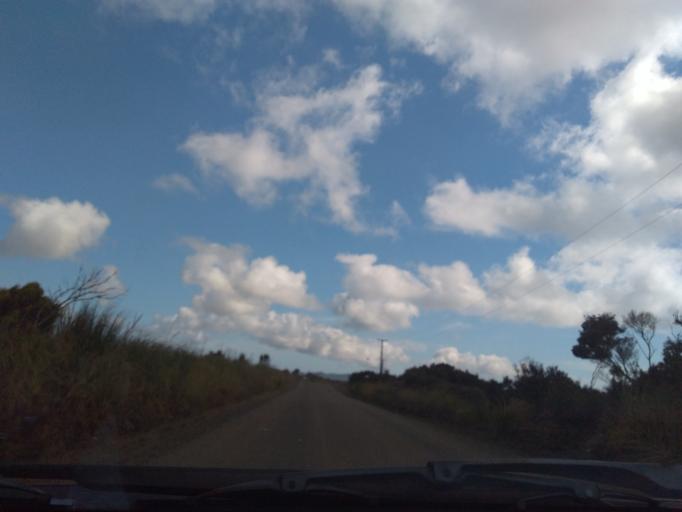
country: NZ
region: Northland
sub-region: Far North District
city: Taipa
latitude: -34.9529
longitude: 173.3736
